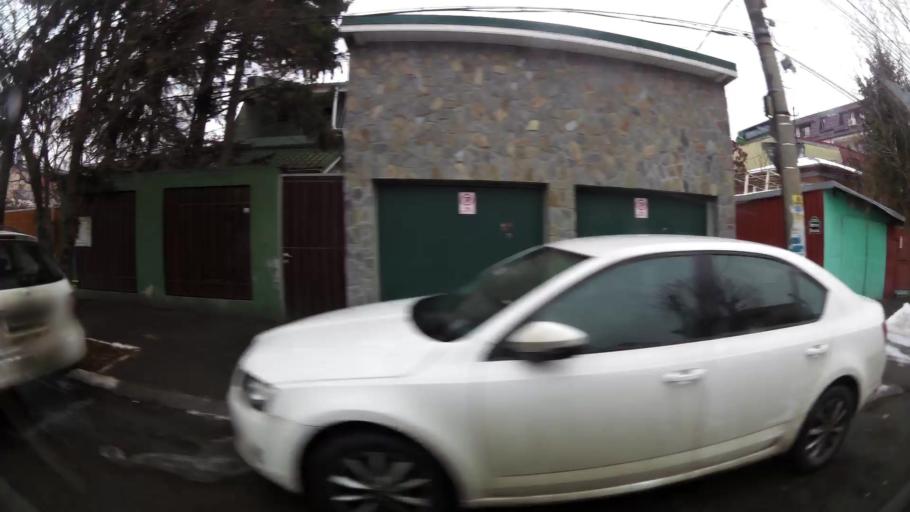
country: RO
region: Ilfov
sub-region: Comuna Chiajna
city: Rosu
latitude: 44.4902
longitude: 26.0436
